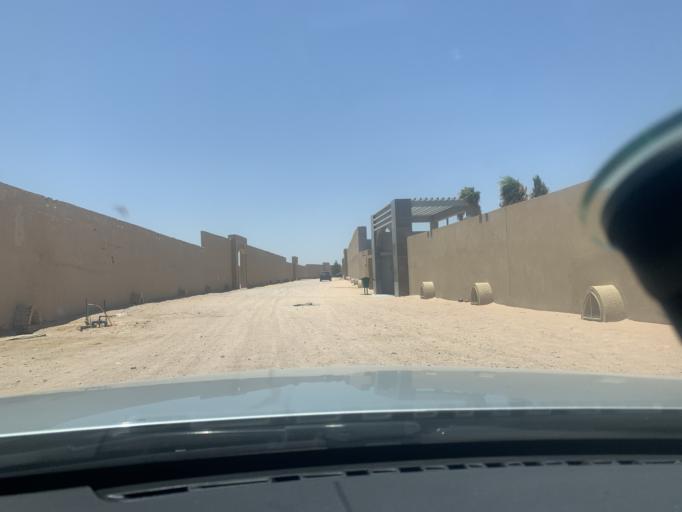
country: EG
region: Red Sea
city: El Gouna
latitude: 27.3949
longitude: 33.6505
